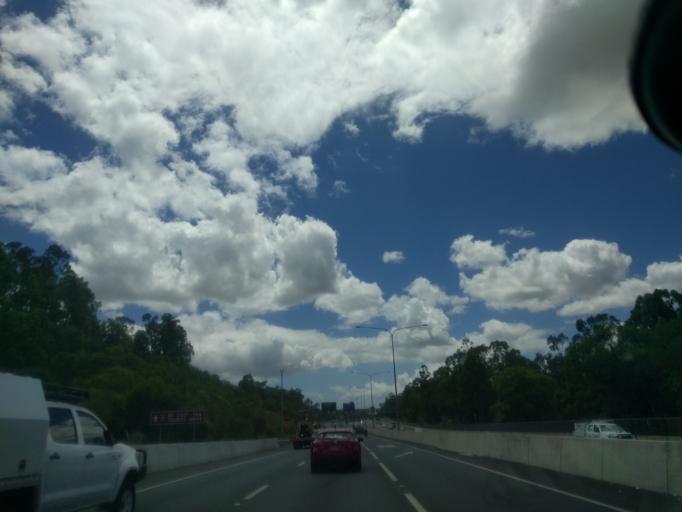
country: AU
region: Queensland
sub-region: Brisbane
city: Taringa
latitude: -27.4823
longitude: 152.9698
